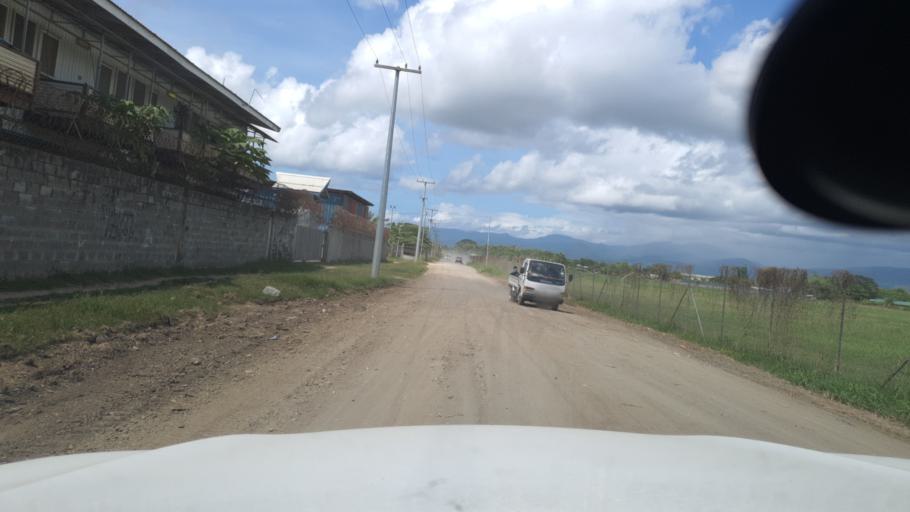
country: SB
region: Guadalcanal
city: Honiara
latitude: -9.4208
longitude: 160.0357
